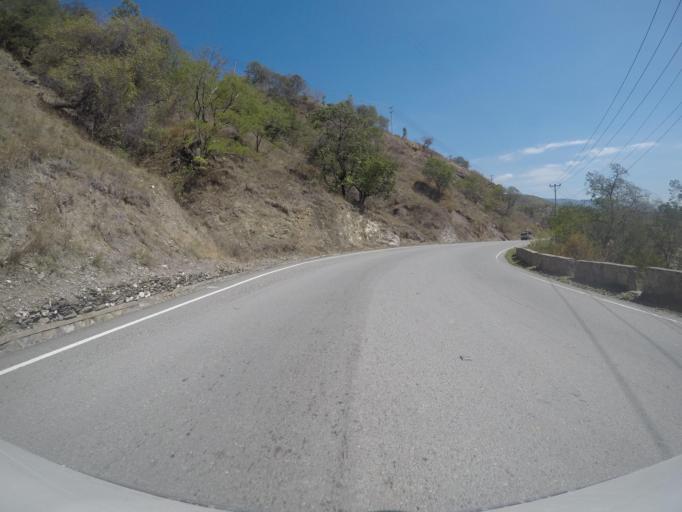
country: TL
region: Liquica
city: Liquica
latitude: -8.5761
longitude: 125.3715
